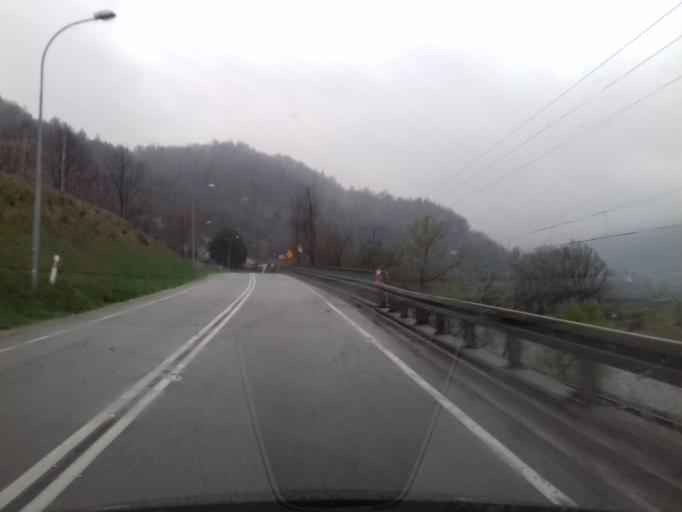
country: PL
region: Lesser Poland Voivodeship
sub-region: Powiat nowosadecki
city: Piwniczna-Zdroj
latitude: 49.4547
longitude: 20.6957
